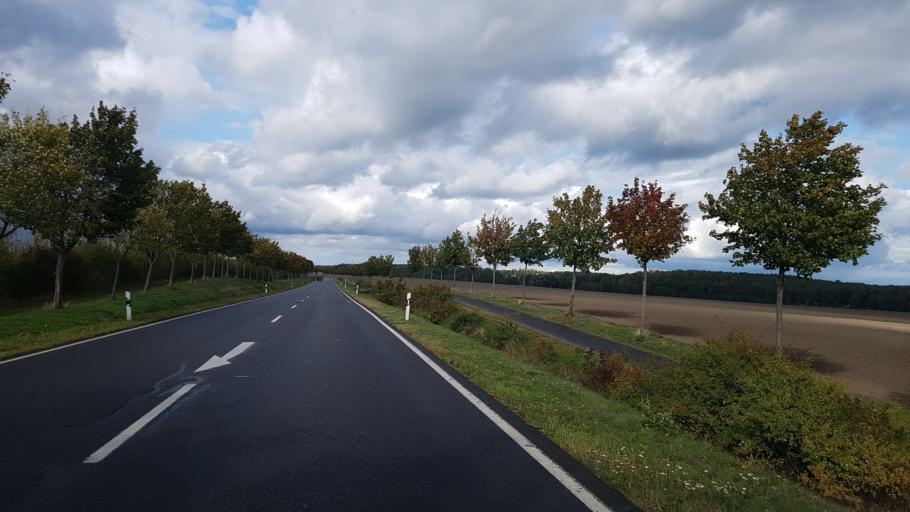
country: DE
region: Saxony
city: Dahlen
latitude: 51.3836
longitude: 12.9912
